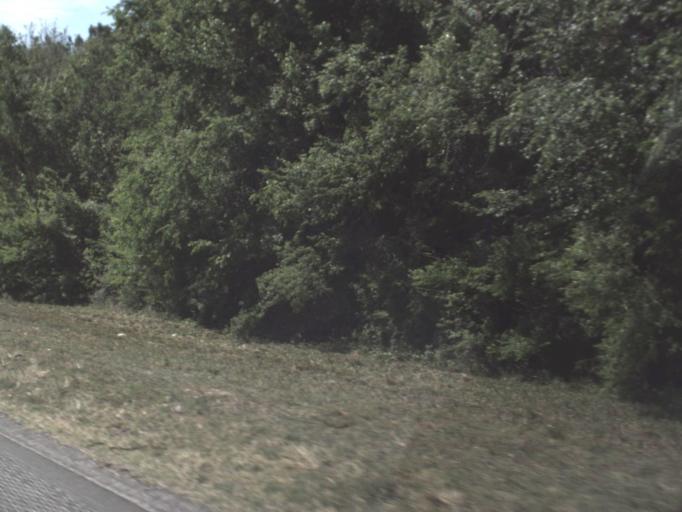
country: US
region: Florida
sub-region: Sumter County
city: Lake Panasoffkee
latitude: 28.7982
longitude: -82.0882
